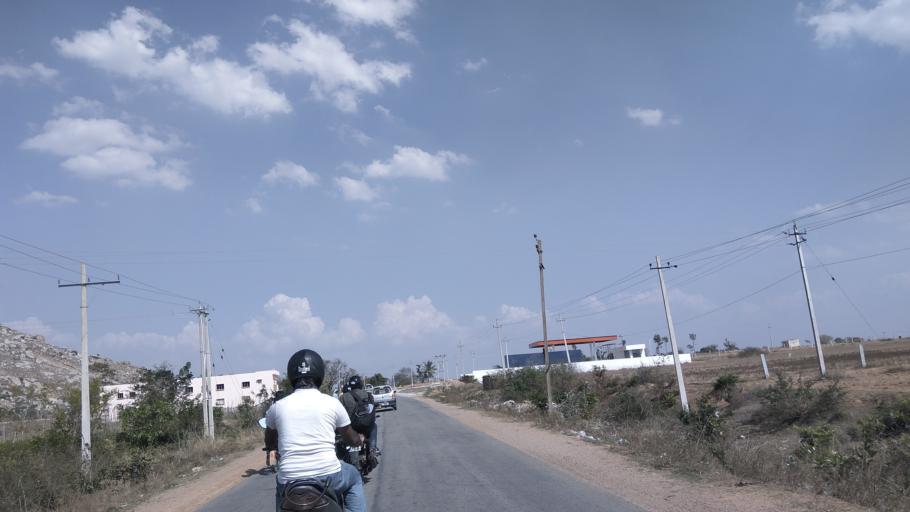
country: IN
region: Karnataka
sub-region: Kolar
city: Mulbagal
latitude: 13.1657
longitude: 78.3688
